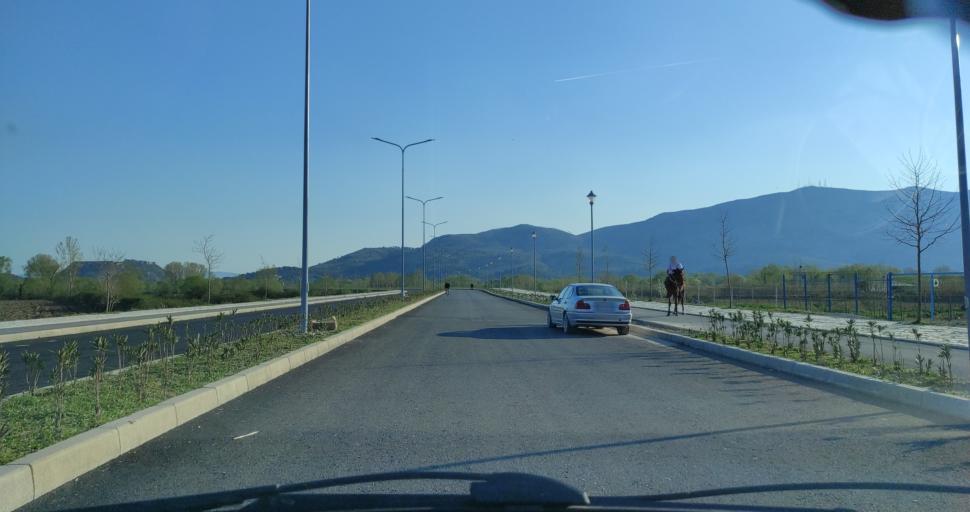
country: AL
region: Shkoder
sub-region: Rrethi i Shkodres
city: Shkoder
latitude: 42.0750
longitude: 19.4905
